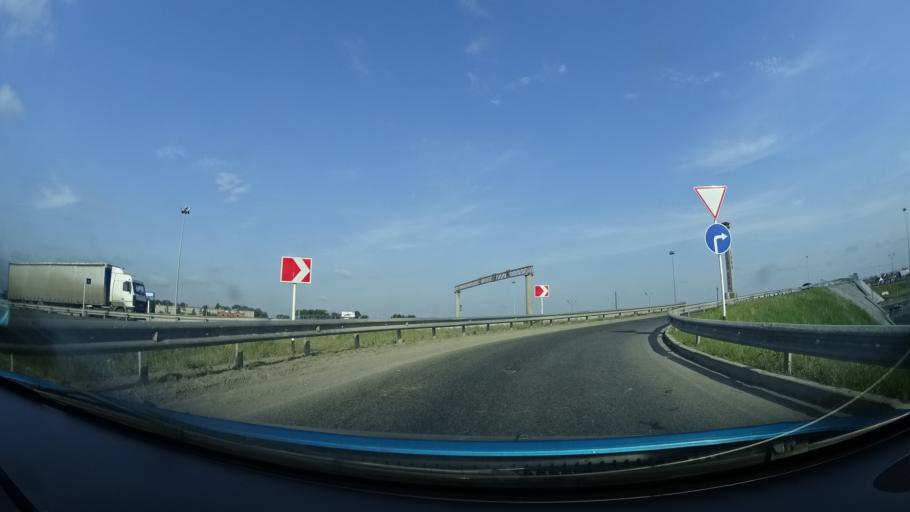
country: RU
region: Perm
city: Kondratovo
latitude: 57.9538
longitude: 56.1235
